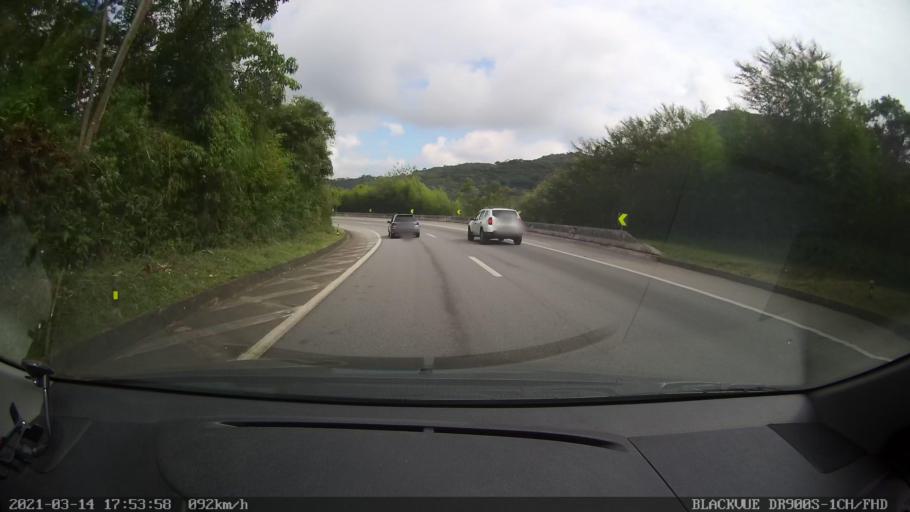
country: BR
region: Rio de Janeiro
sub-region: Petropolis
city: Petropolis
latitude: -22.4846
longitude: -43.2308
